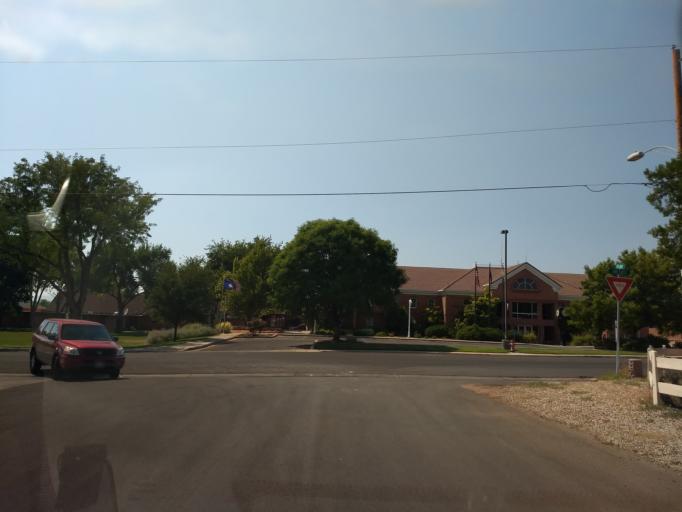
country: US
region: Utah
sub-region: Washington County
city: Washington
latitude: 37.1315
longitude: -113.5079
